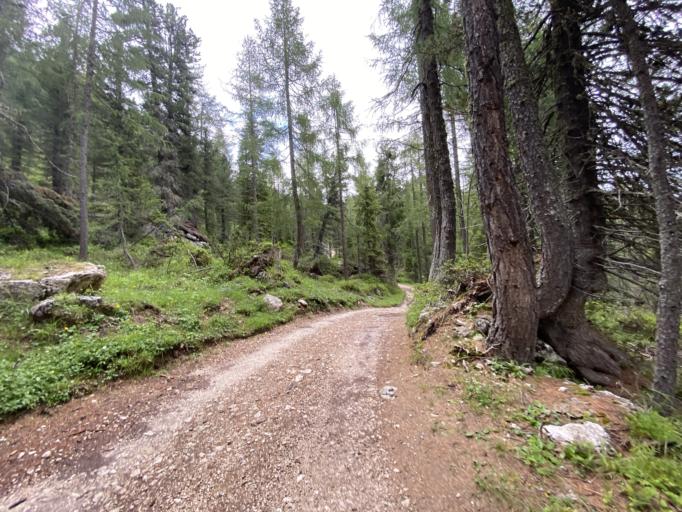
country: IT
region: Veneto
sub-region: Provincia di Belluno
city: Cortina d'Ampezzo
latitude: 46.4839
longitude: 12.1103
